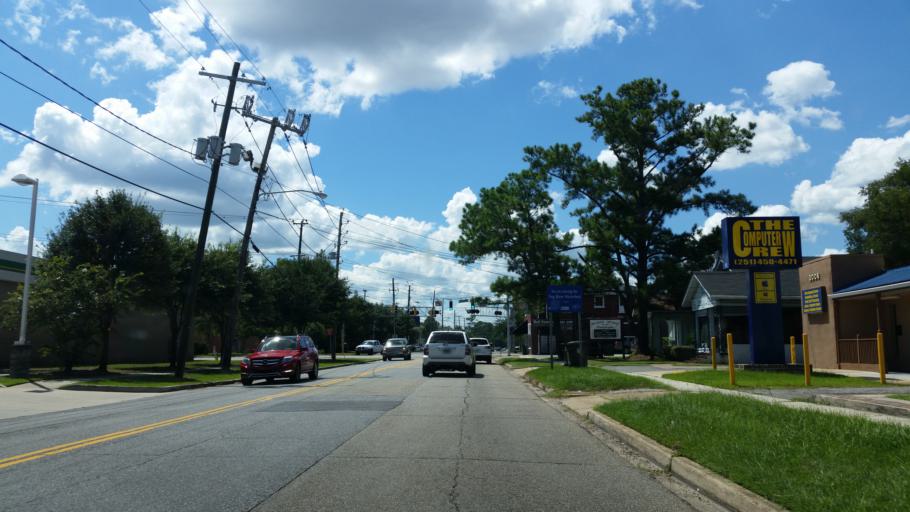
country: US
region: Alabama
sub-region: Mobile County
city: Mobile
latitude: 30.6766
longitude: -88.0872
